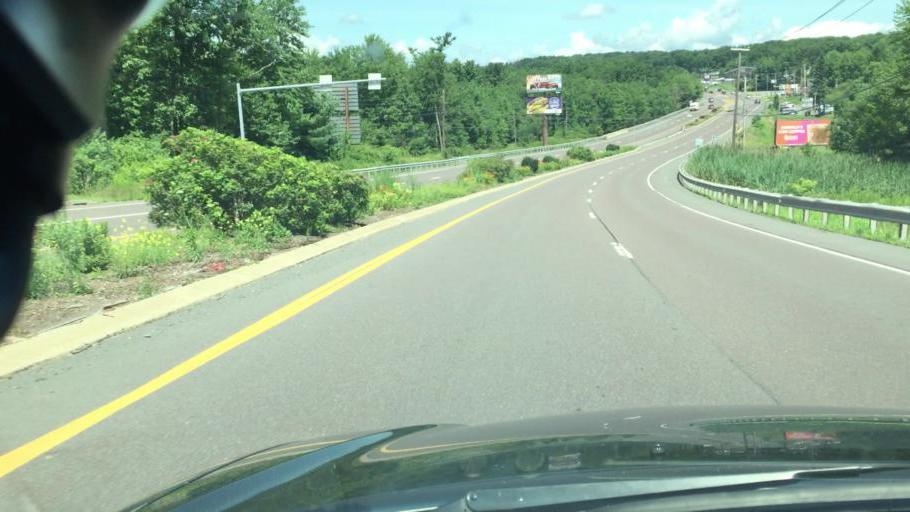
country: US
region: Pennsylvania
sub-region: Luzerne County
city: West Hazleton
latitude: 40.9715
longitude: -76.0107
